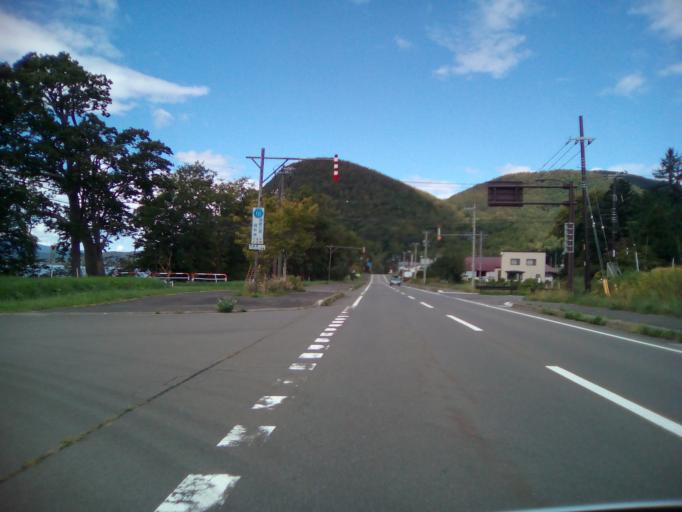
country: JP
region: Hokkaido
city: Date
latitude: 42.6149
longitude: 140.9155
